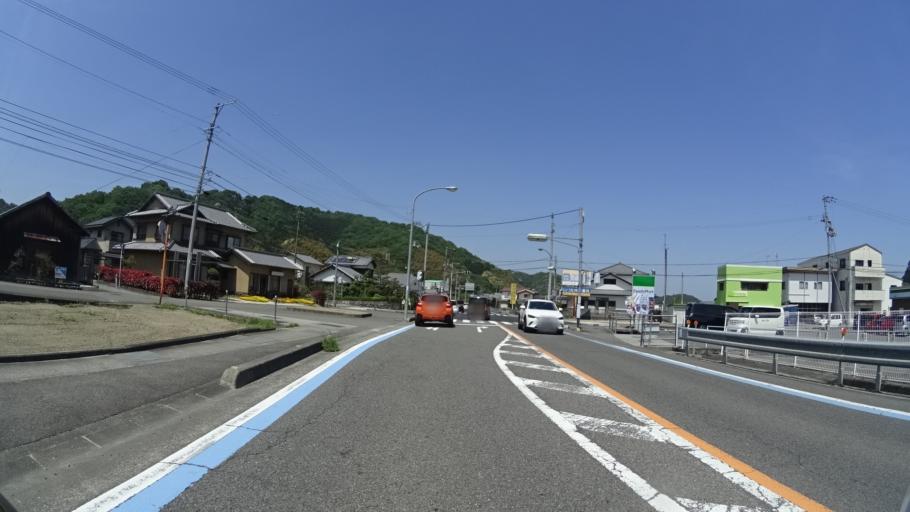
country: JP
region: Ehime
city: Hojo
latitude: 34.0200
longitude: 132.9415
